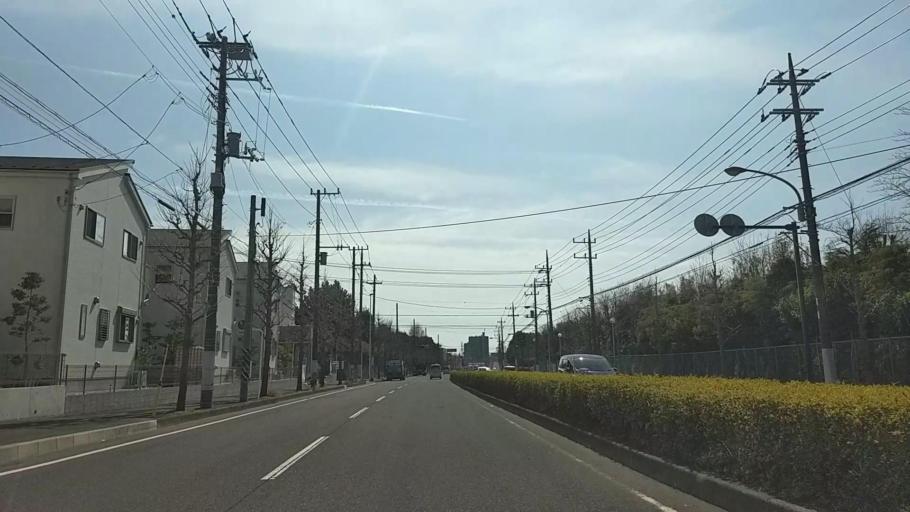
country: JP
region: Kanagawa
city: Fujisawa
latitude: 35.3862
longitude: 139.4571
